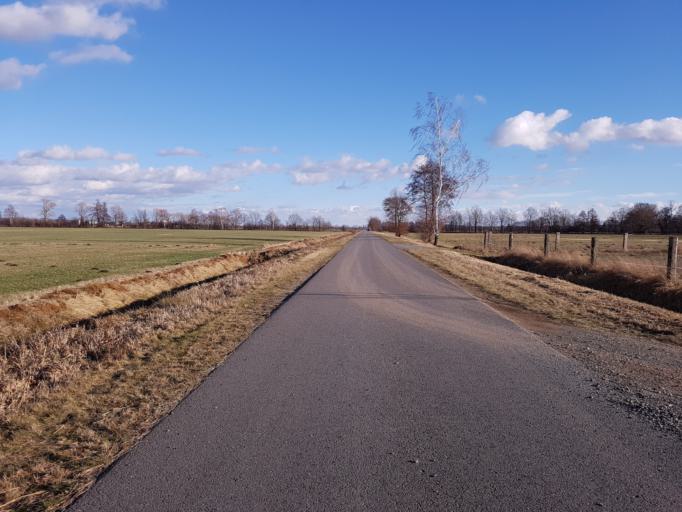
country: DE
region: Brandenburg
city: Groden
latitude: 51.4138
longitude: 13.5712
